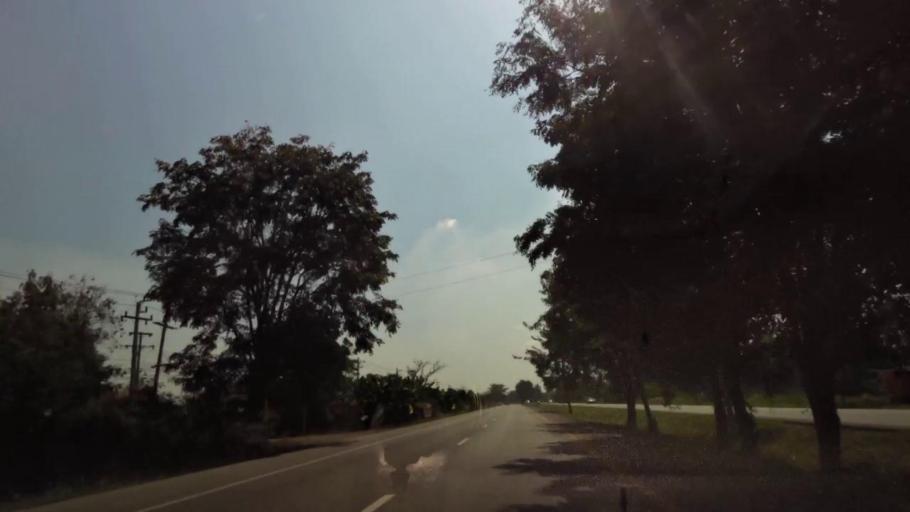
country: TH
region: Phichit
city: Bueng Na Rang
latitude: 16.2405
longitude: 100.1254
